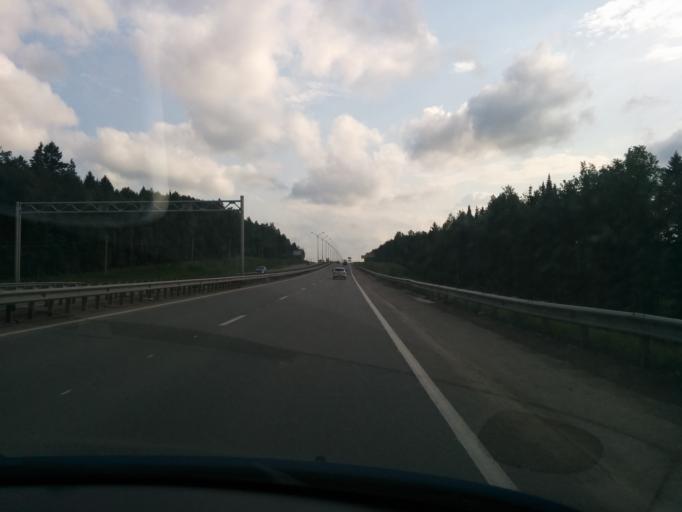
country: RU
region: Perm
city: Ferma
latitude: 58.0098
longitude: 56.3990
